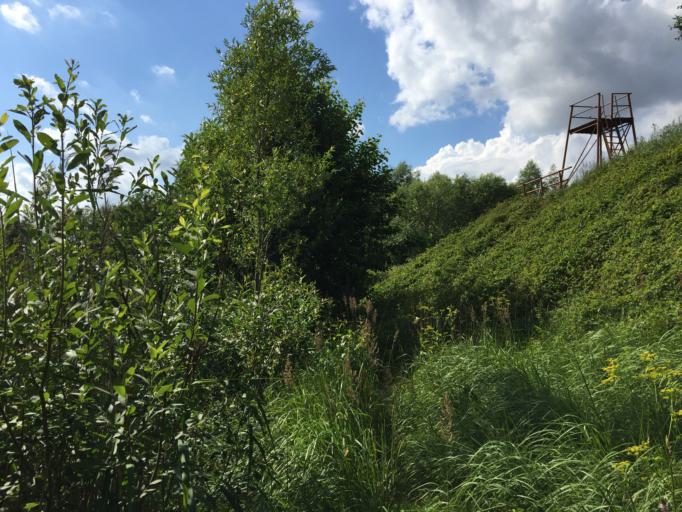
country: LV
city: Tervete
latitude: 56.6157
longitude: 23.4455
